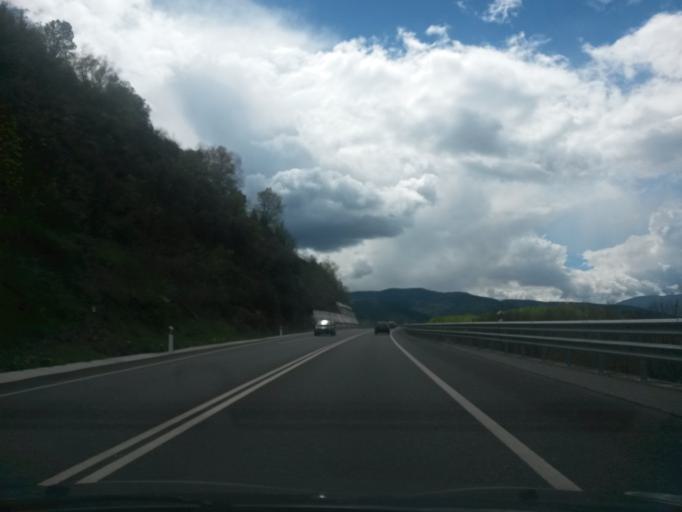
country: ES
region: Catalonia
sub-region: Provincia de Lleida
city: la Seu d'Urgell
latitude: 42.3685
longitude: 1.4553
